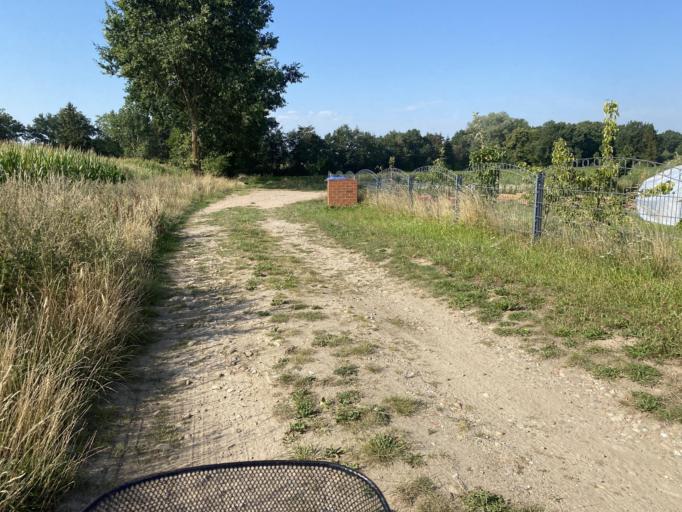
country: DE
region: Lower Saxony
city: Dahlenburg
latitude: 53.1689
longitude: 10.7263
